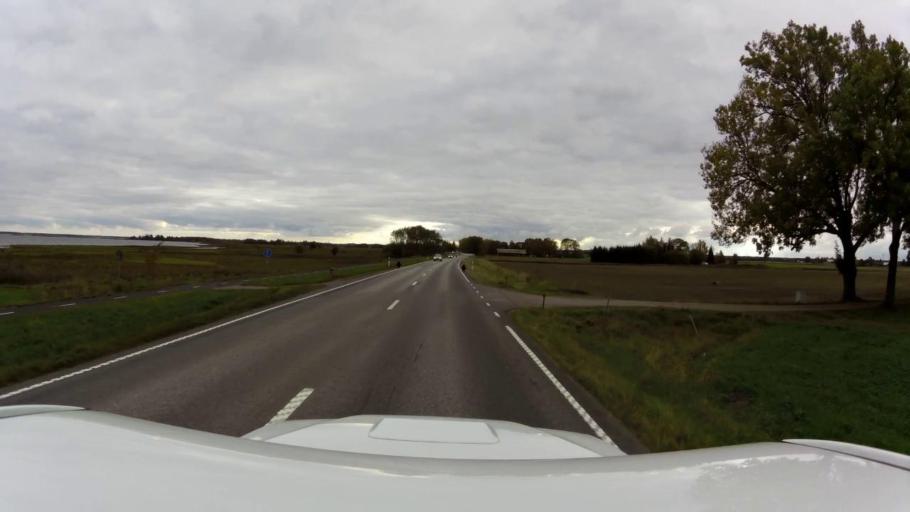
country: SE
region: OEstergoetland
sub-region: Linkopings Kommun
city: Berg
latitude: 58.4730
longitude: 15.5276
